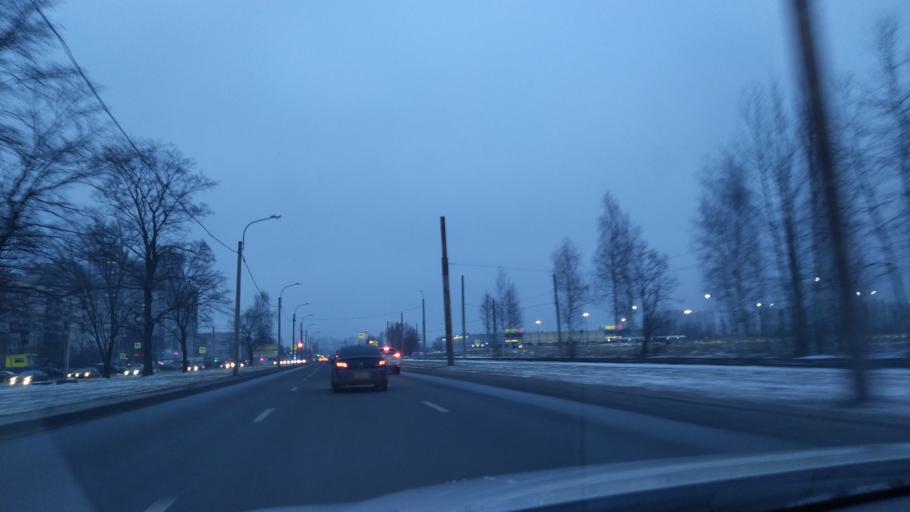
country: RU
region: Leningrad
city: Murino
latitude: 60.0273
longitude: 30.4325
